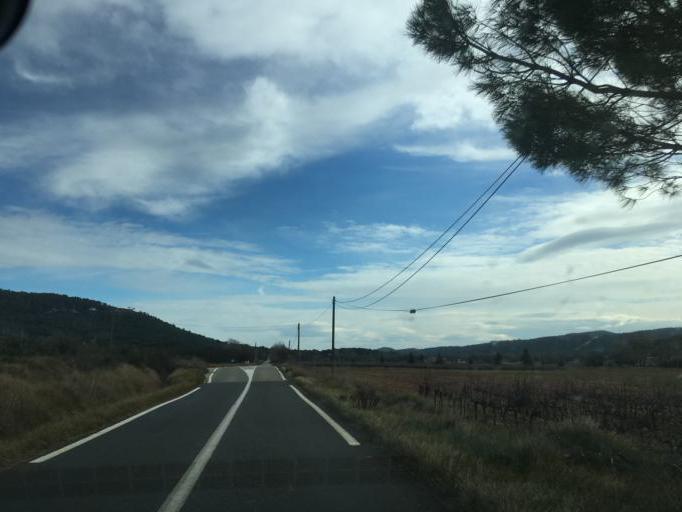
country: FR
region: Provence-Alpes-Cote d'Azur
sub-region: Departement du Var
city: Bras
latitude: 43.4468
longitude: 6.0007
